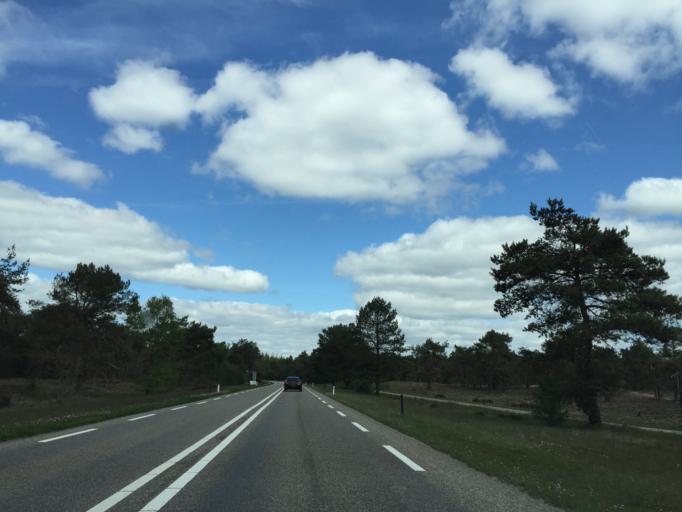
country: NL
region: Gelderland
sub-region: Gemeente Apeldoorn
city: Uddel
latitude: 52.2093
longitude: 5.7797
